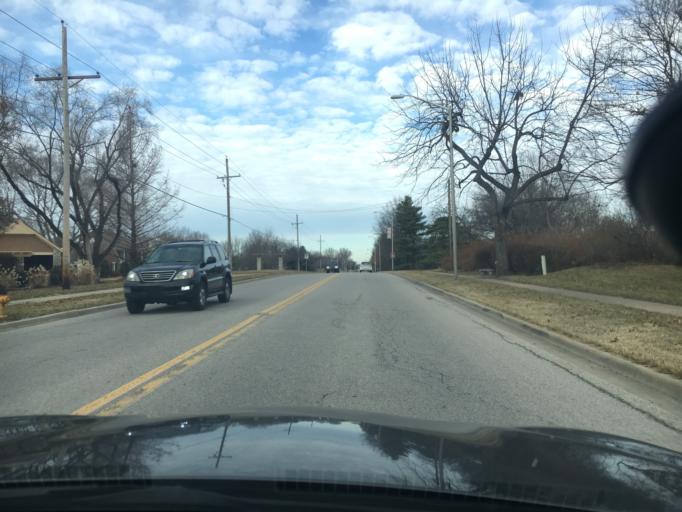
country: US
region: Kansas
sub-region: Johnson County
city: Leawood
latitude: 38.8907
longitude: -94.6305
